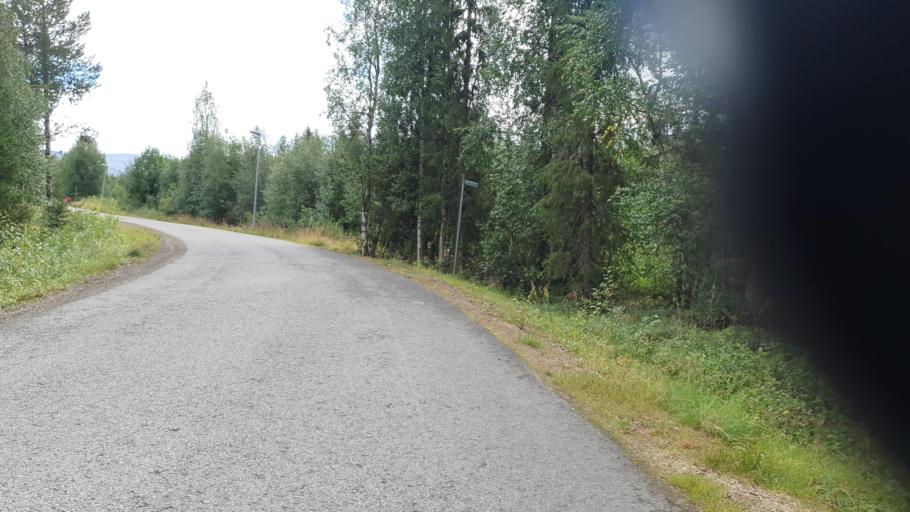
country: FI
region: Lapland
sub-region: Tunturi-Lappi
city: Kolari
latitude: 67.6201
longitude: 24.1468
